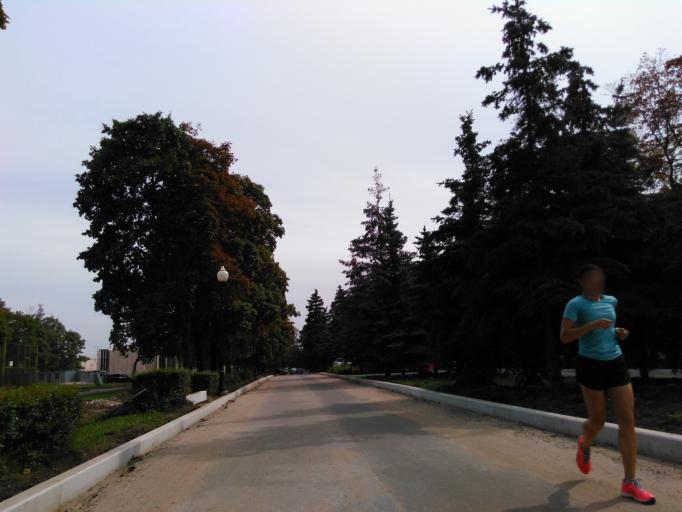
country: RU
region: Moscow
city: Luzhniki
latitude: 55.7224
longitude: 37.5501
